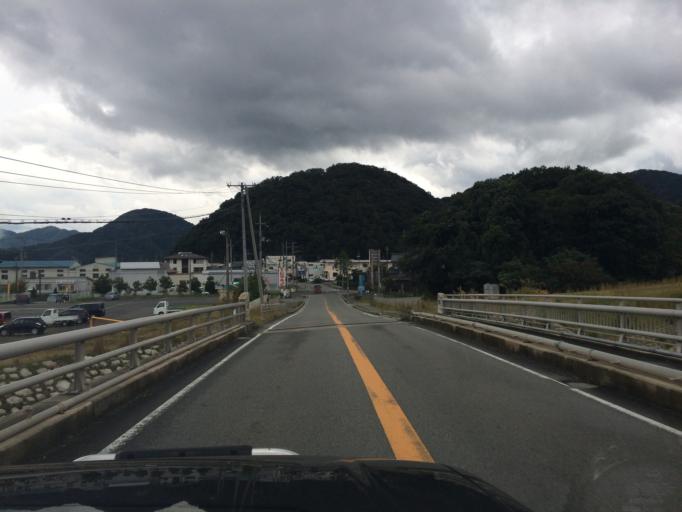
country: JP
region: Hyogo
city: Toyooka
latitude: 35.4573
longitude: 134.7727
